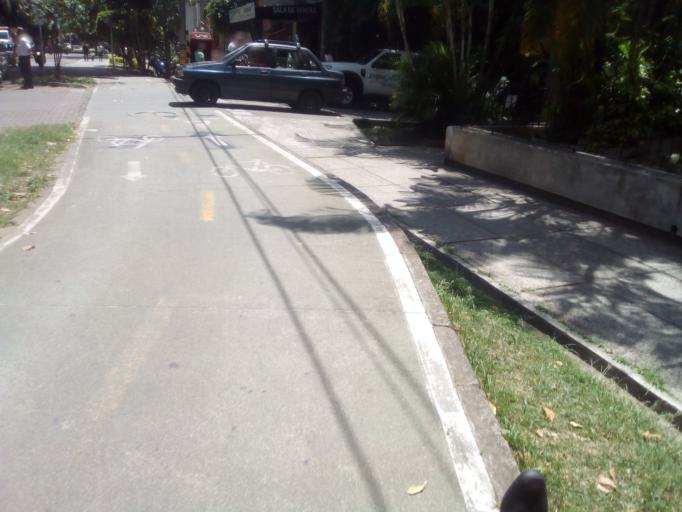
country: CO
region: Antioquia
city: Medellin
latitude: 6.2481
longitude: -75.5936
